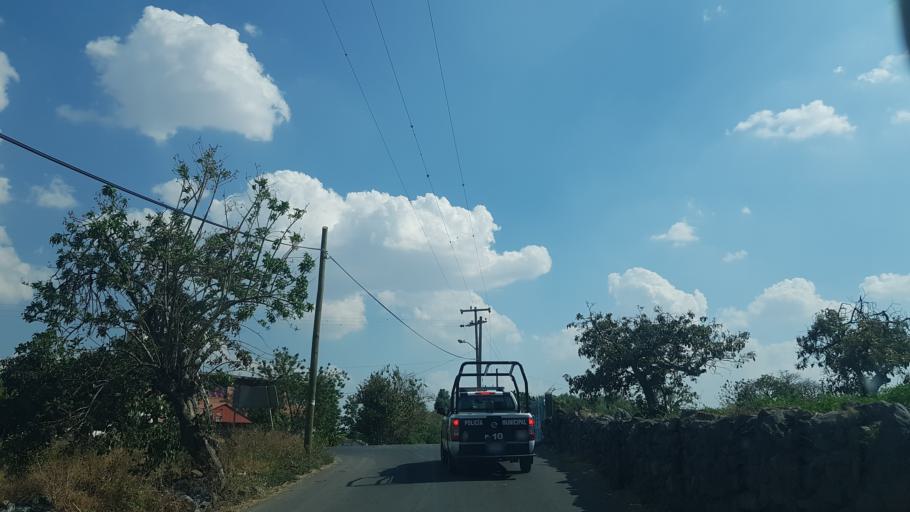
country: MX
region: Puebla
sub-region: Atlixco
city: Colonia Agricola de Ocotepec (Colonia San Jose)
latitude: 18.9214
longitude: -98.5411
